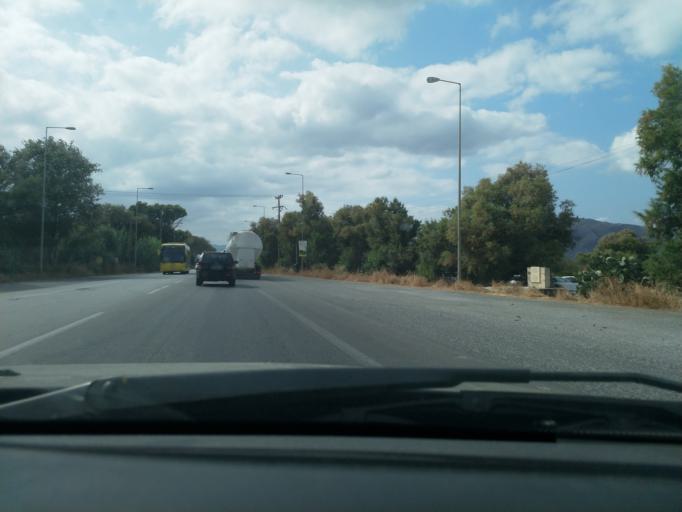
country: GR
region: Crete
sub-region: Nomos Chanias
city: Georgioupolis
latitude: 35.3547
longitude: 24.2799
